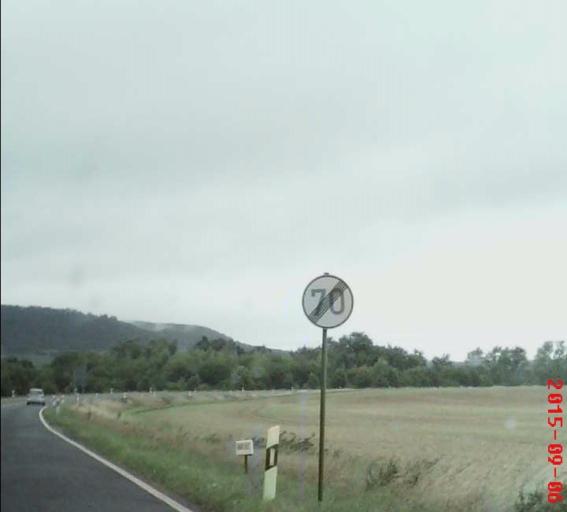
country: DE
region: Thuringia
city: Breitenworbis
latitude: 51.4030
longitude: 10.4340
